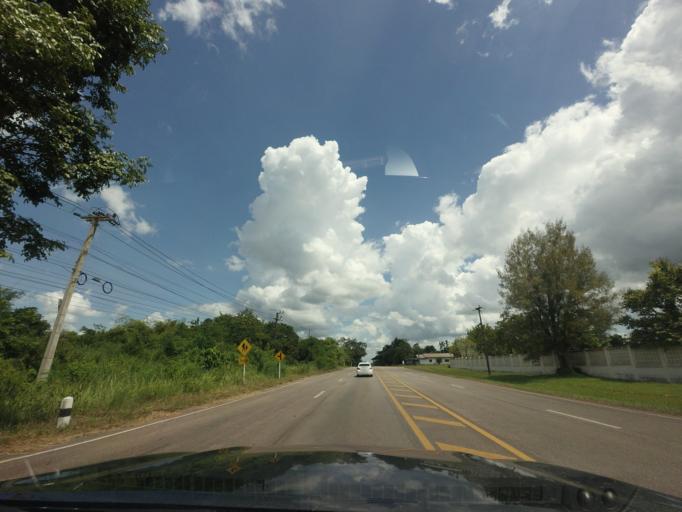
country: TH
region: Changwat Udon Thani
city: Ban Dung
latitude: 17.6863
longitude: 103.2015
